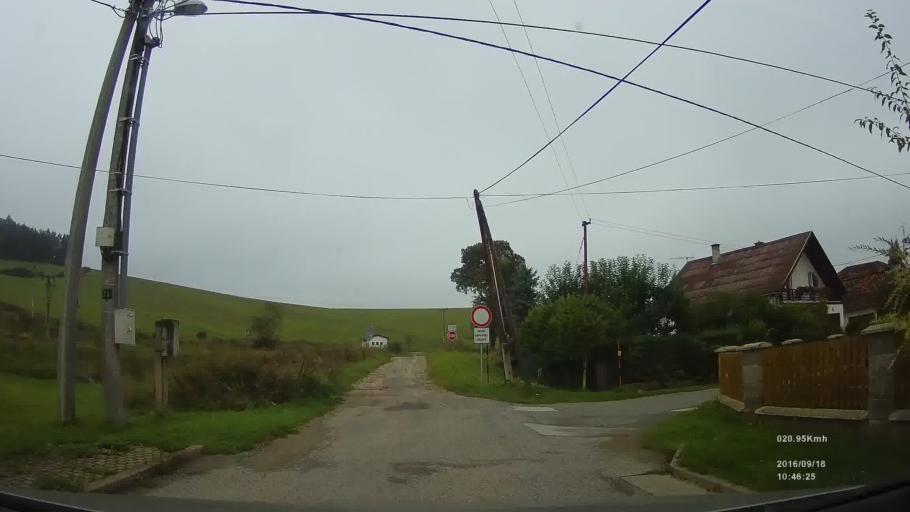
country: SK
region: Kosicky
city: Spisska Nova Ves
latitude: 48.9653
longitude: 20.5777
